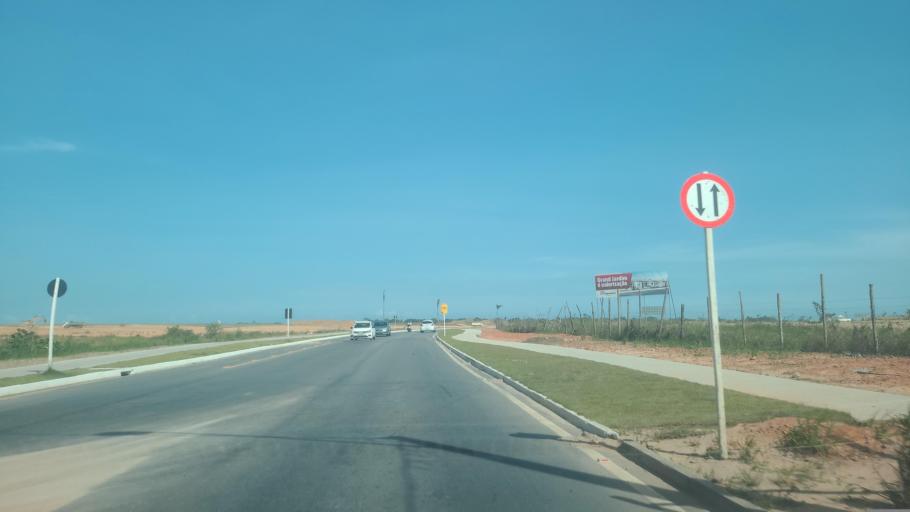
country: BR
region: Alagoas
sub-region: Satuba
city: Satuba
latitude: -9.5324
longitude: -35.7694
